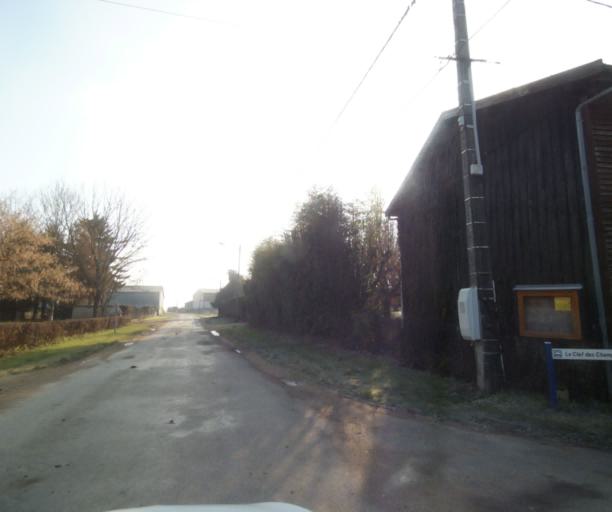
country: FR
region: Champagne-Ardenne
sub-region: Departement de la Haute-Marne
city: Montier-en-Der
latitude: 48.4963
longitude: 4.7239
